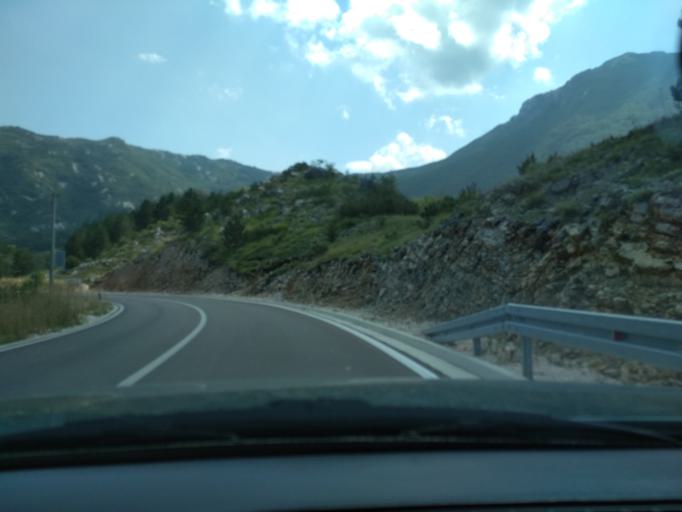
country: ME
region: Kotor
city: Kotor
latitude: 42.4278
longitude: 18.8169
